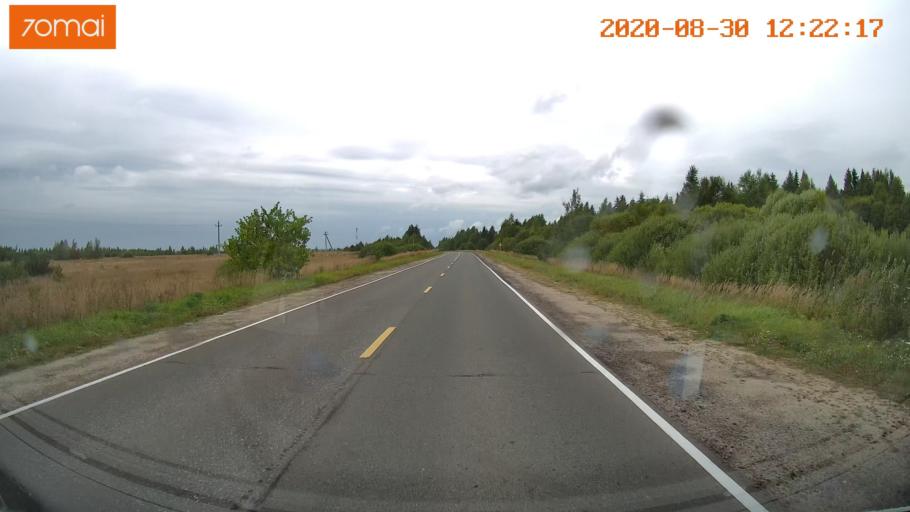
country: RU
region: Ivanovo
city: Yur'yevets
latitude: 57.3290
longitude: 42.8544
